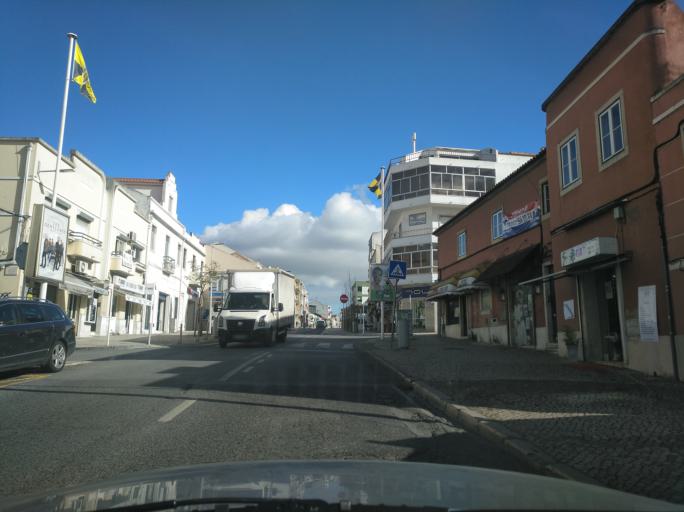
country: PT
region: Lisbon
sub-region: Loures
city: Loures
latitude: 38.8316
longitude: -9.1696
